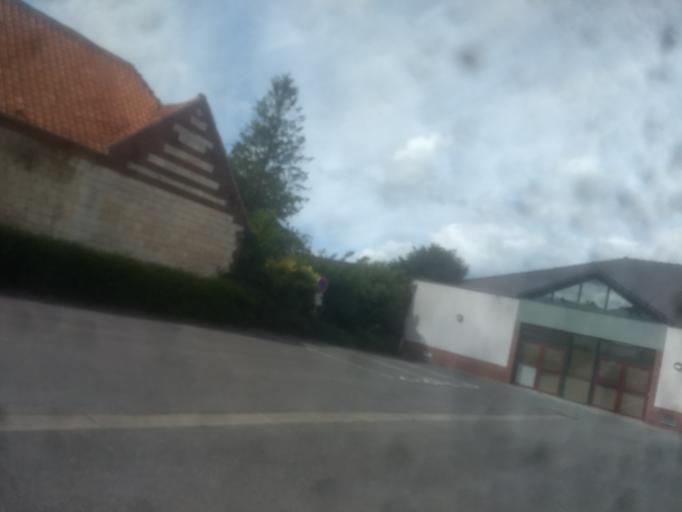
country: FR
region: Nord-Pas-de-Calais
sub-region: Departement du Pas-de-Calais
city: Duisans
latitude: 50.3289
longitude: 2.6382
